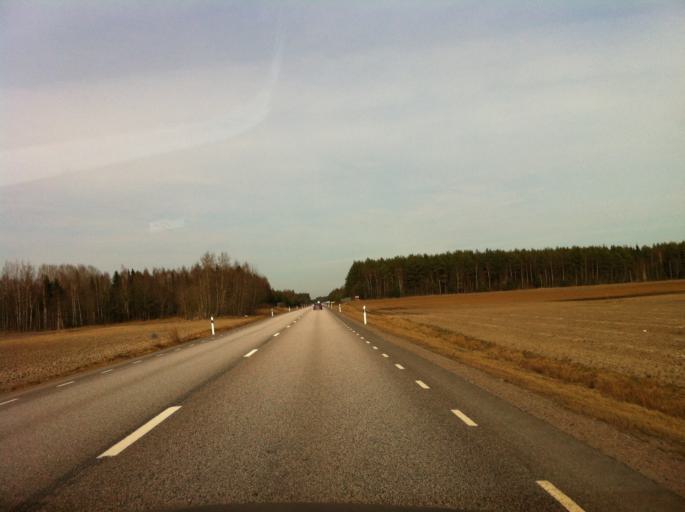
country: SE
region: Vaestra Goetaland
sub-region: Toreboda Kommun
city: Toereboda
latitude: 58.8077
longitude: 13.9769
